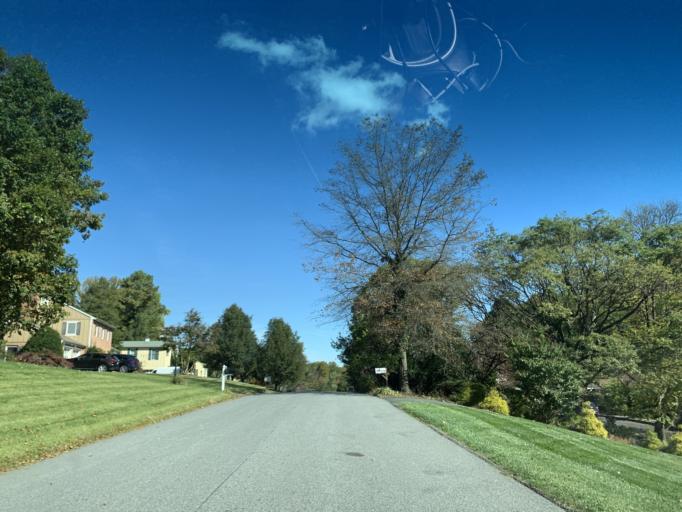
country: US
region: Maryland
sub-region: Harford County
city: Bel Air South
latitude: 39.5194
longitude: -76.3254
